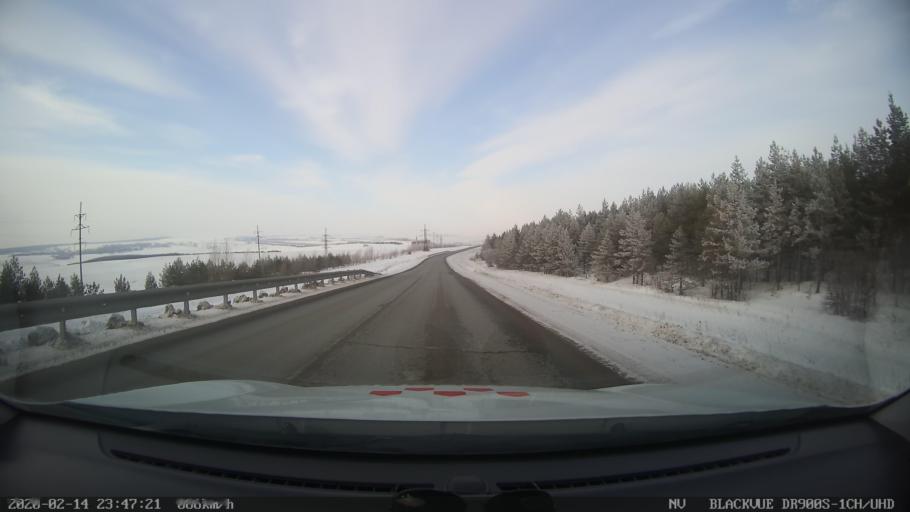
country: RU
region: Tatarstan
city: Kuybyshevskiy Zaton
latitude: 55.2377
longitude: 49.2097
